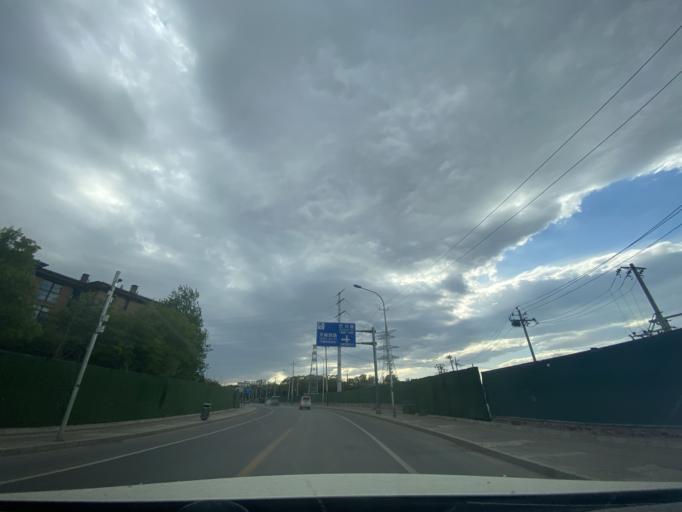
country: CN
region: Beijing
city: Haidian
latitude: 39.9726
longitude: 116.2837
